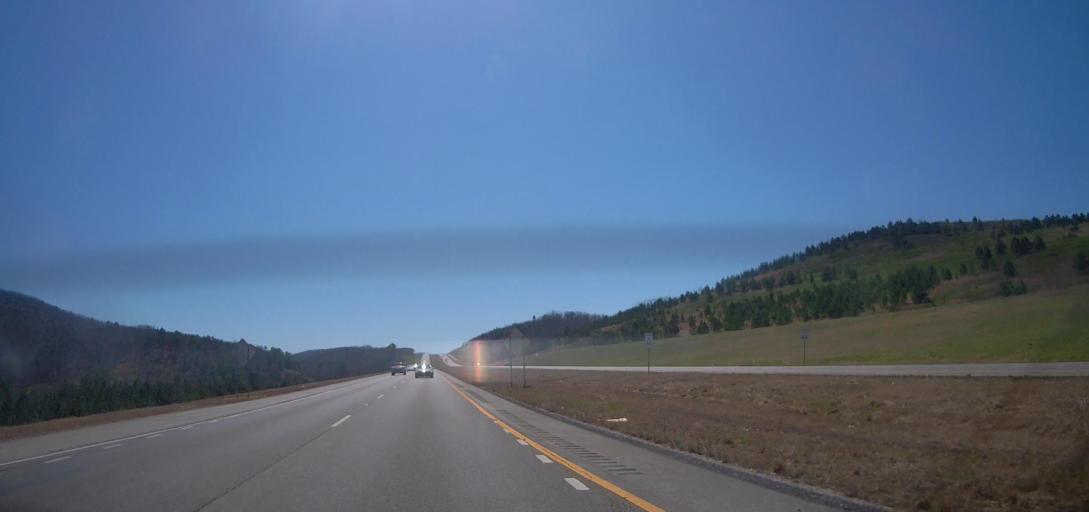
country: US
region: Alabama
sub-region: Calhoun County
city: Saks
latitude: 33.6982
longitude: -85.8077
